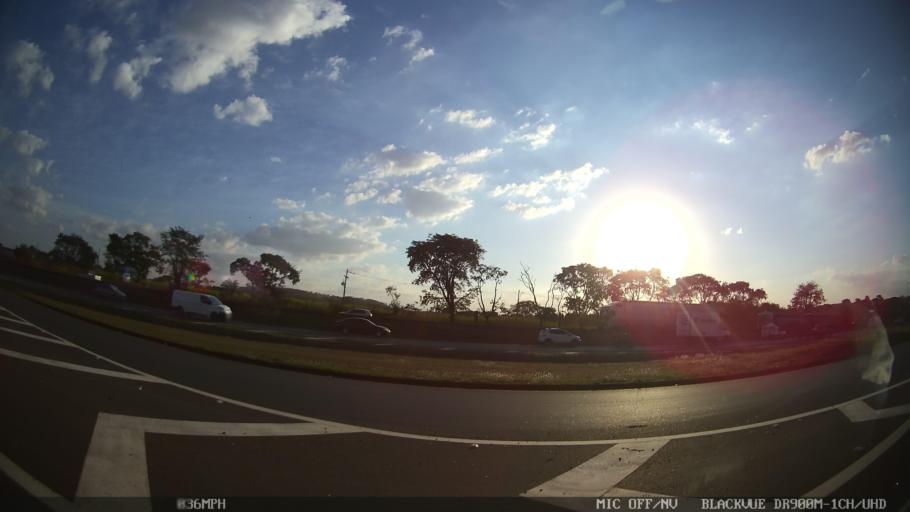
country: BR
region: Sao Paulo
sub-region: Ribeirao Preto
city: Ribeirao Preto
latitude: -21.1619
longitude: -47.7558
